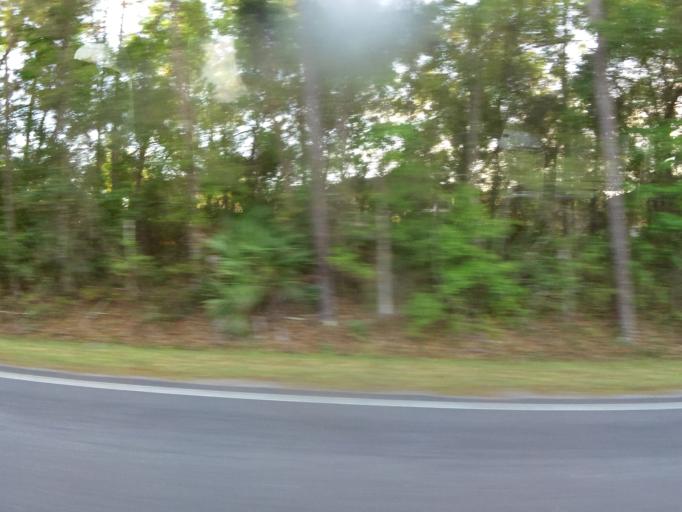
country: US
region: Florida
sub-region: Saint Johns County
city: Fruit Cove
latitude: 30.1243
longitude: -81.5877
